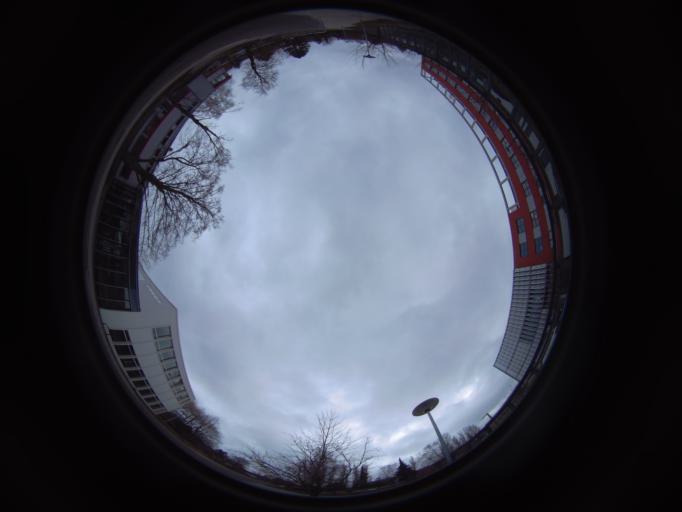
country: DE
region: Mecklenburg-Vorpommern
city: Rostock
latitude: 54.0786
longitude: 12.1125
